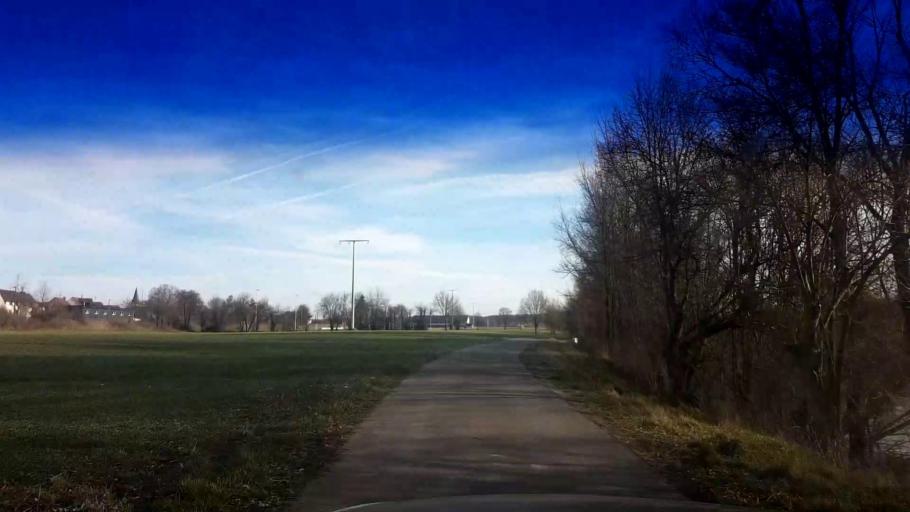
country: DE
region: Bavaria
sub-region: Regierungsbezirk Unterfranken
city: Stettfeld
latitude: 49.9472
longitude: 10.7439
